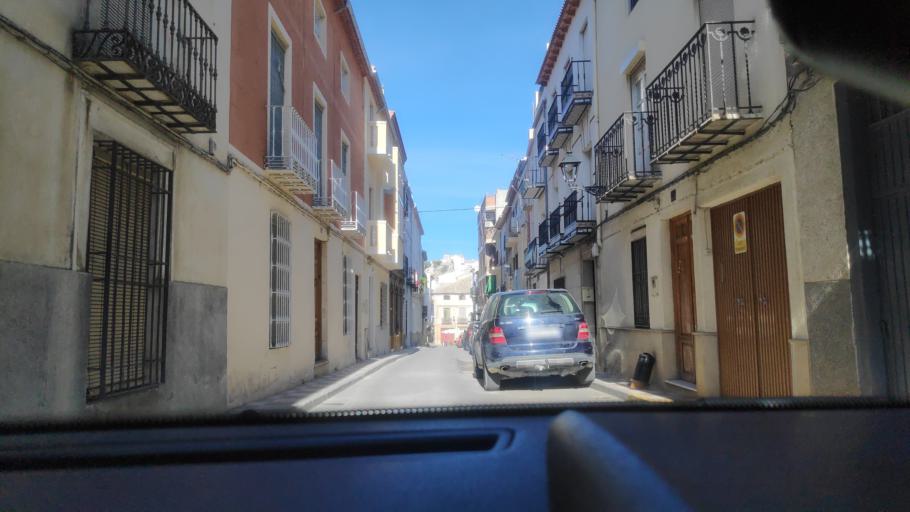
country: ES
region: Andalusia
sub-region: Provincia de Jaen
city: Torres
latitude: 37.7845
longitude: -3.5079
